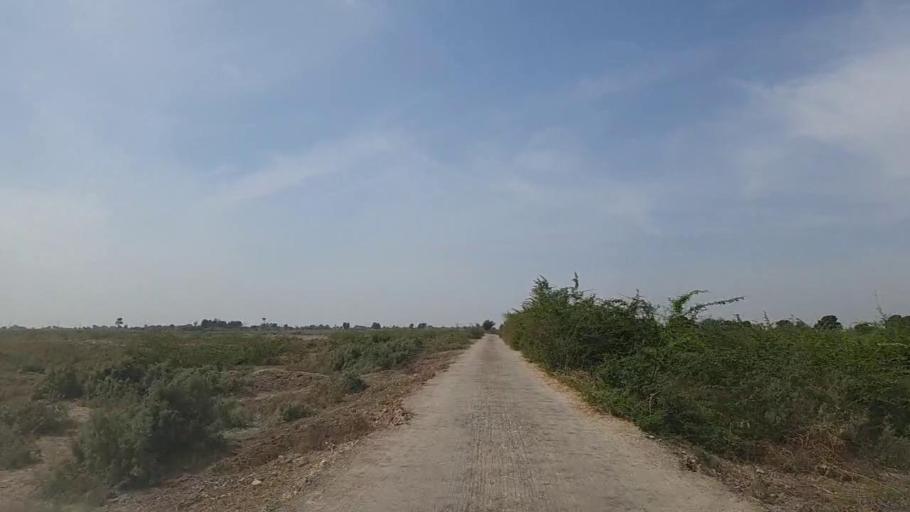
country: PK
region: Sindh
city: Kunri
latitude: 25.2129
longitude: 69.4754
